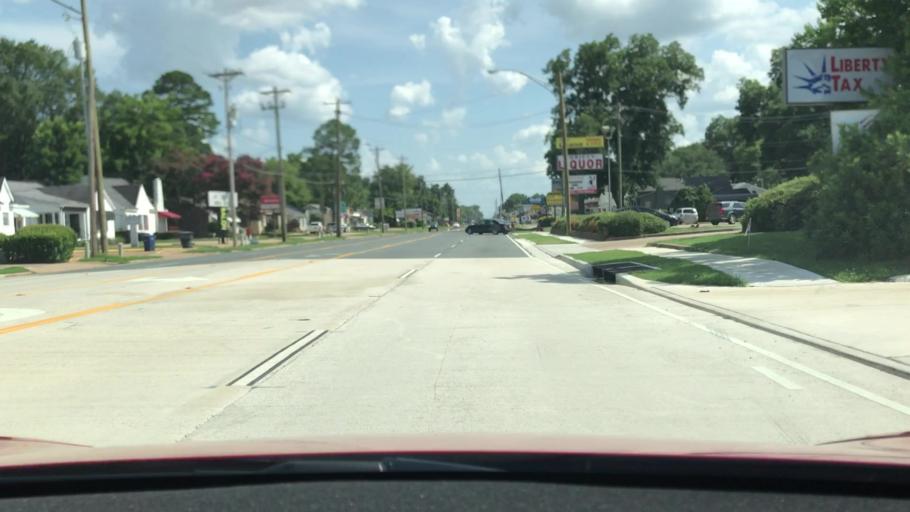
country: US
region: Louisiana
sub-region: Bossier Parish
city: Bossier City
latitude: 32.4774
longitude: -93.7223
